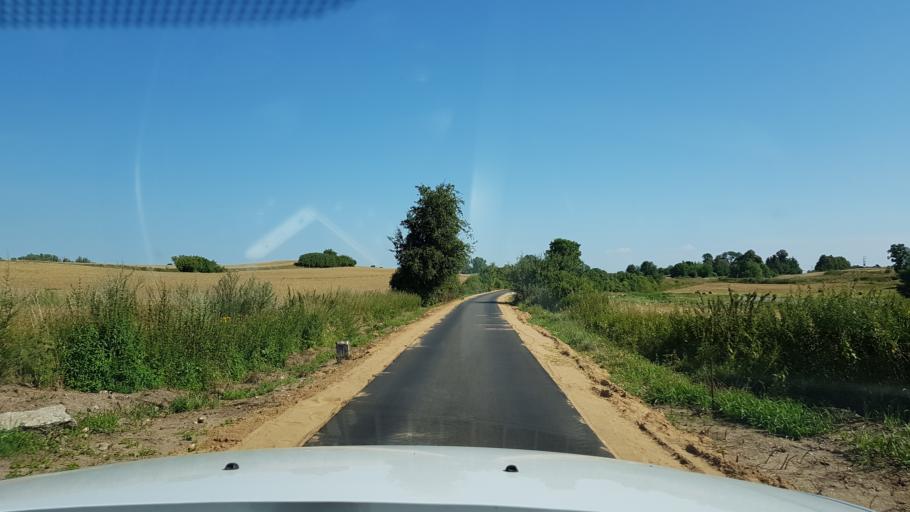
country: PL
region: West Pomeranian Voivodeship
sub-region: Powiat gryfinski
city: Cedynia
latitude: 52.8587
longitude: 14.2836
